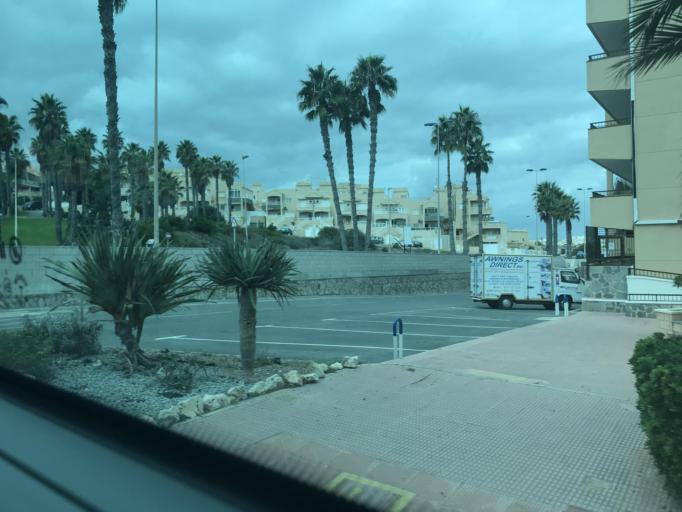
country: ES
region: Valencia
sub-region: Provincia de Alicante
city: Torrevieja
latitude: 38.0051
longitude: -0.6501
